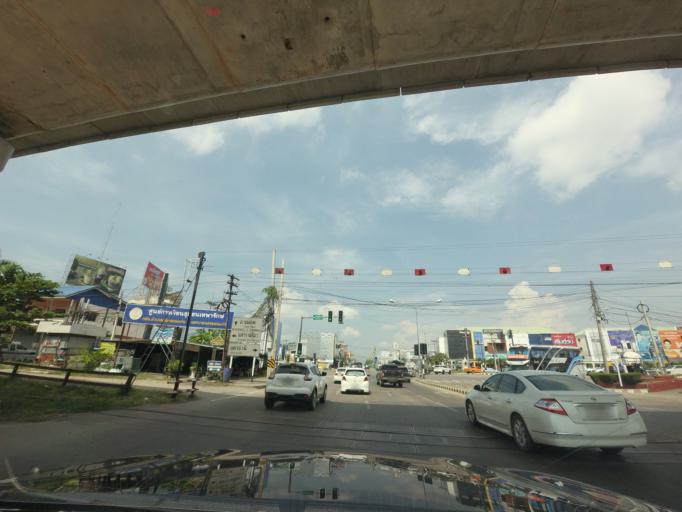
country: TH
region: Khon Kaen
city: Khon Kaen
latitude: 16.4394
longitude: 102.8292
